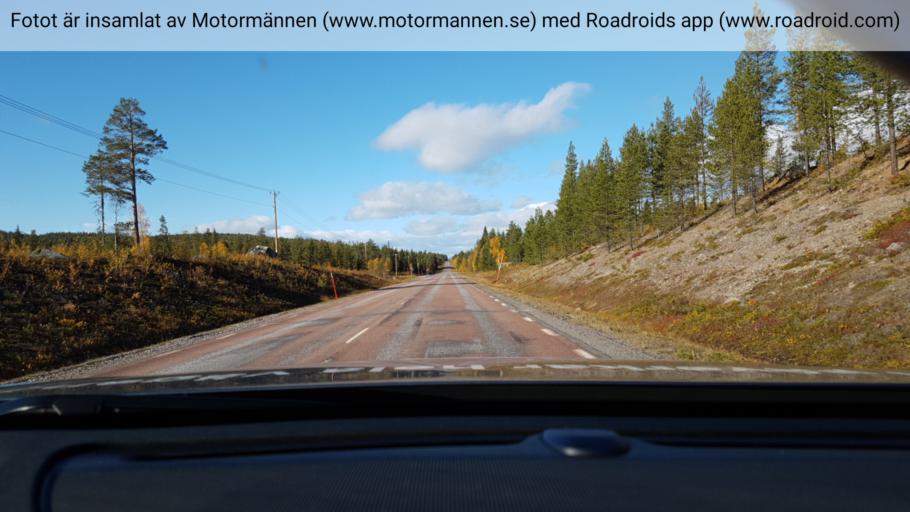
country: SE
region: Norrbotten
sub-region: Arjeplogs Kommun
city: Arjeplog
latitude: 66.0526
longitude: 18.0090
